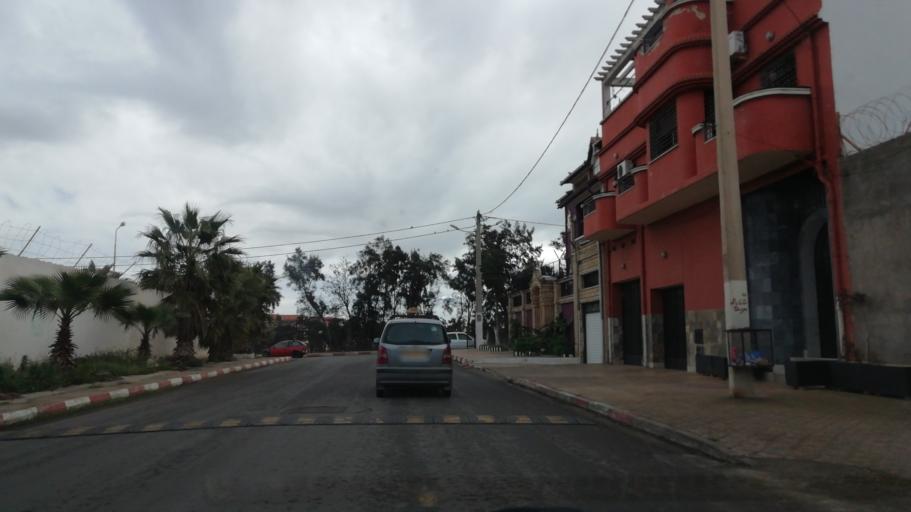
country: DZ
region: Oran
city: Oran
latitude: 35.6952
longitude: -0.5983
